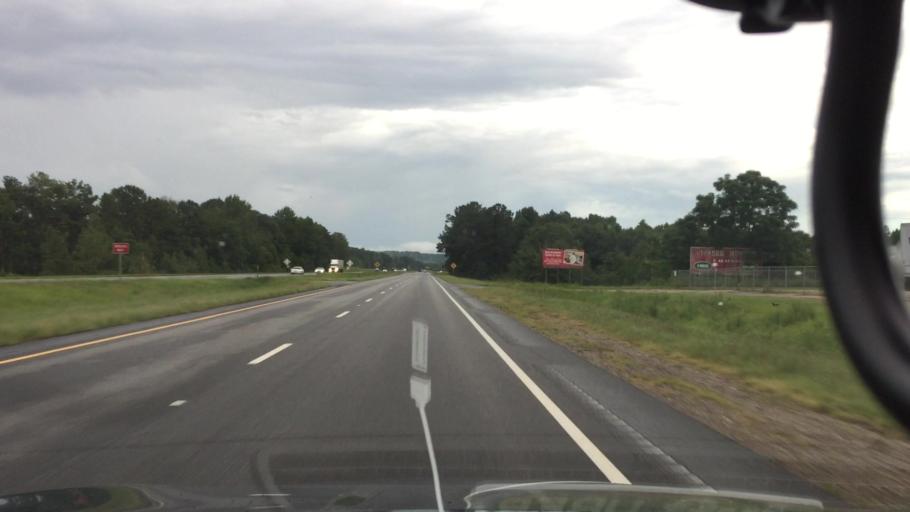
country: US
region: Alabama
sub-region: Pike County
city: Troy
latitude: 31.8824
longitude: -86.0057
